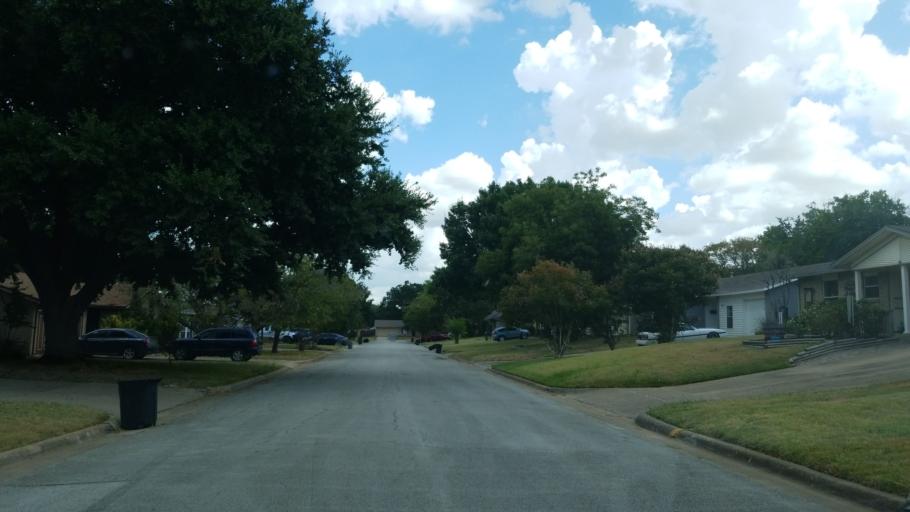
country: US
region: Texas
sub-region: Tarrant County
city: Euless
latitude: 32.8578
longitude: -97.0922
